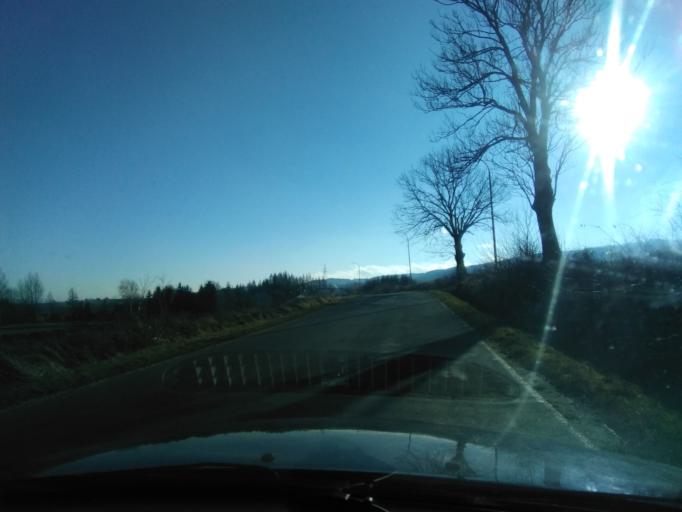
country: PL
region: Subcarpathian Voivodeship
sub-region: Powiat krosnienski
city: Rymanow
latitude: 49.5668
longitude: 21.8879
